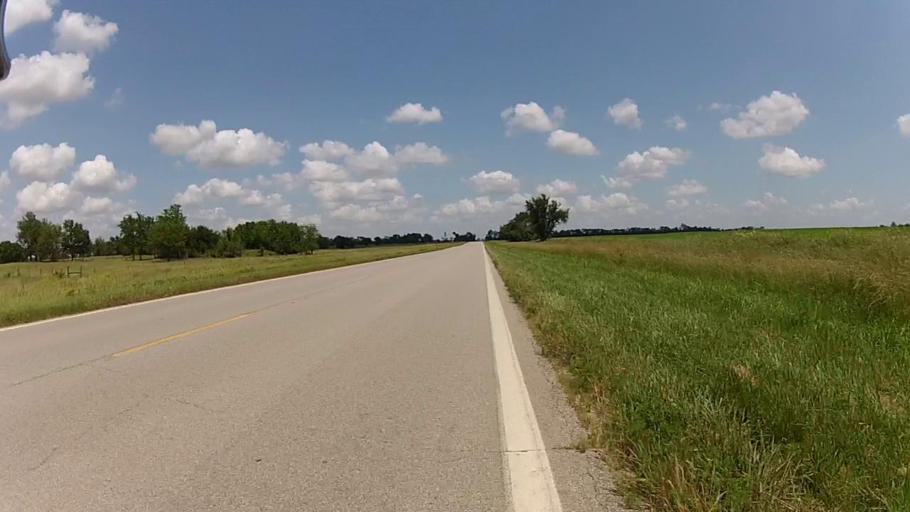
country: US
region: Kansas
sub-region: Labette County
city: Altamont
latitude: 37.1926
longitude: -95.3749
